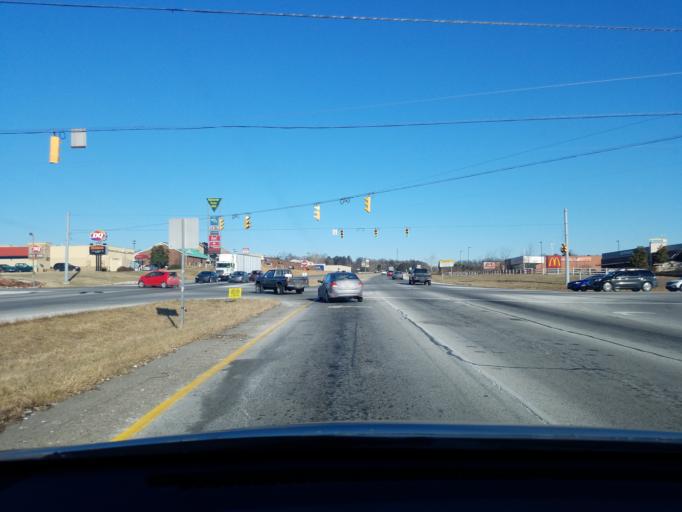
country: US
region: Indiana
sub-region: Floyd County
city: Galena
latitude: 38.3140
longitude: -85.8975
